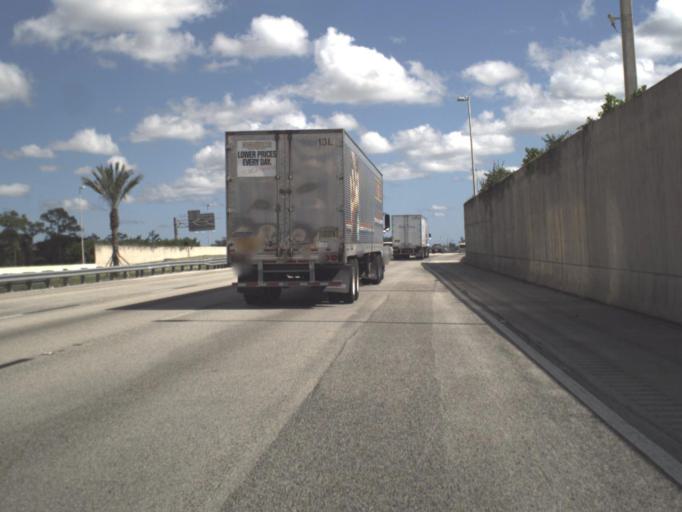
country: US
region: Florida
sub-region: Broward County
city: Parkland
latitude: 26.3015
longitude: -80.2377
